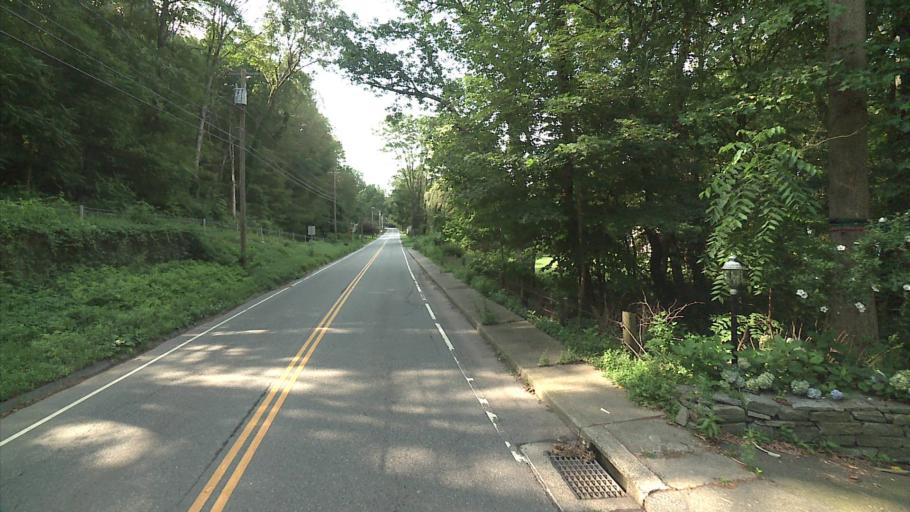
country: US
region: Connecticut
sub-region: Middlesex County
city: East Haddam
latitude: 41.4613
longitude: -72.4640
